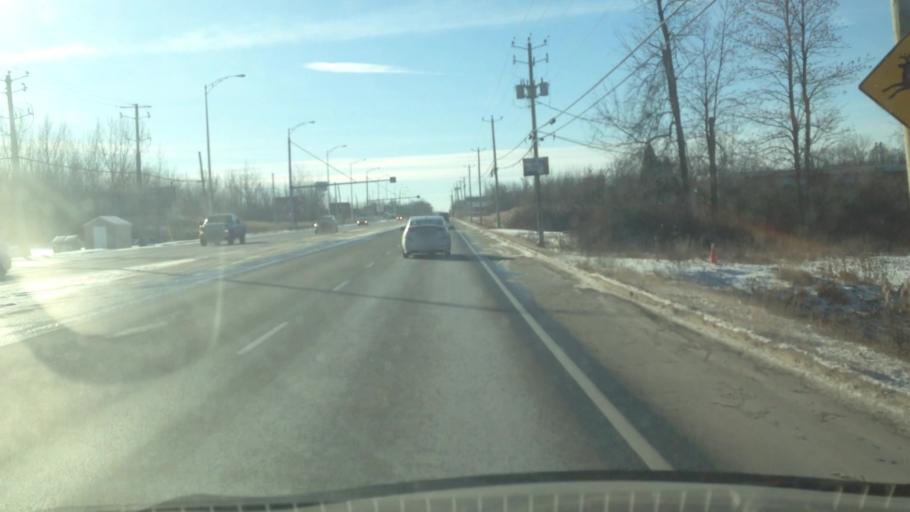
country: CA
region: Quebec
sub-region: Monteregie
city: Chateauguay
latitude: 45.3924
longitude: -73.6964
